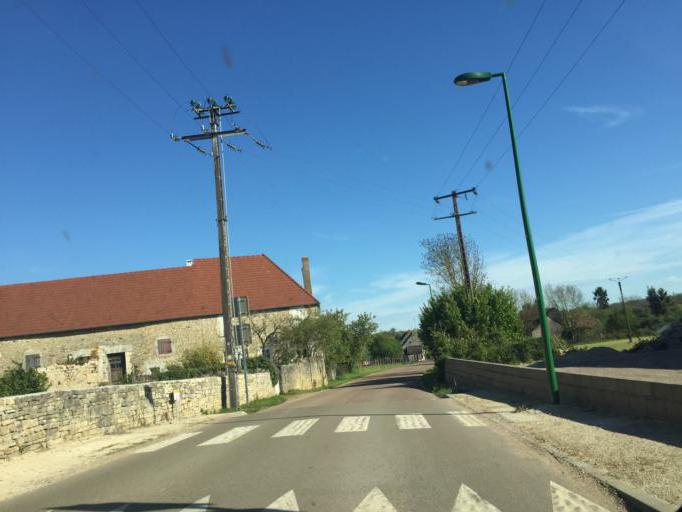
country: FR
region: Bourgogne
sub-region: Departement de la Nievre
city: Clamecy
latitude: 47.4785
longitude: 3.5216
